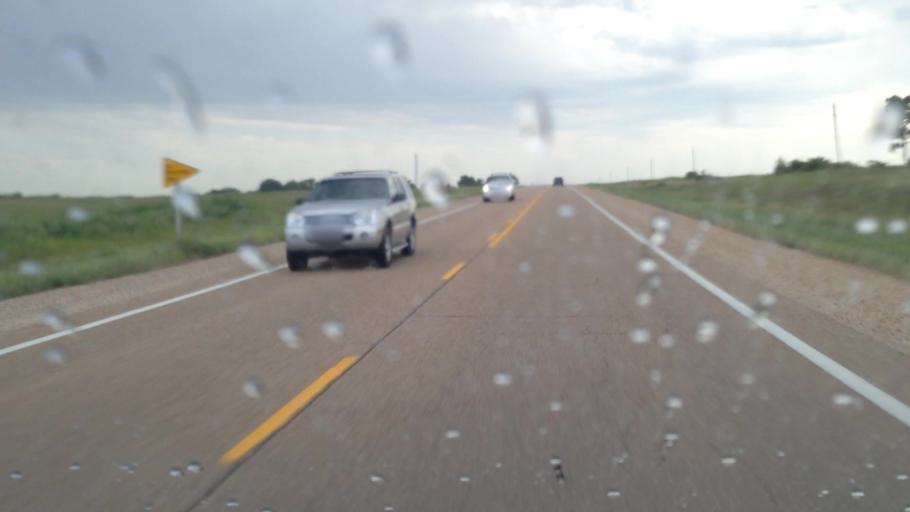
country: US
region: Kansas
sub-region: Coffey County
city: Burlington
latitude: 38.1467
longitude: -95.7392
